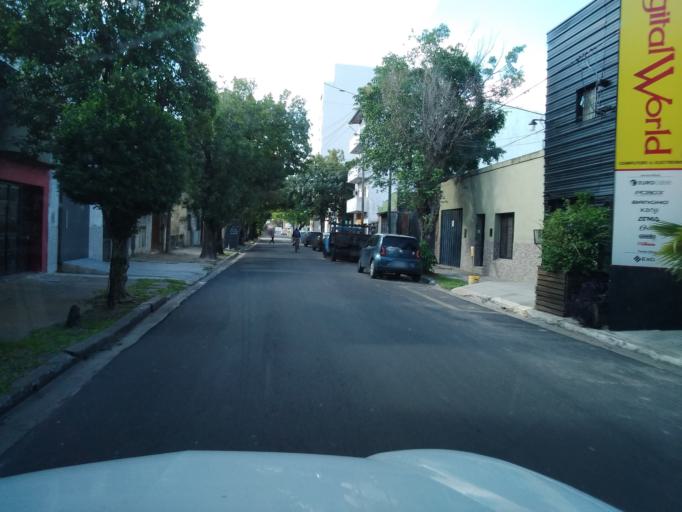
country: AR
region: Corrientes
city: Corrientes
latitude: -27.4780
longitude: -58.8368
